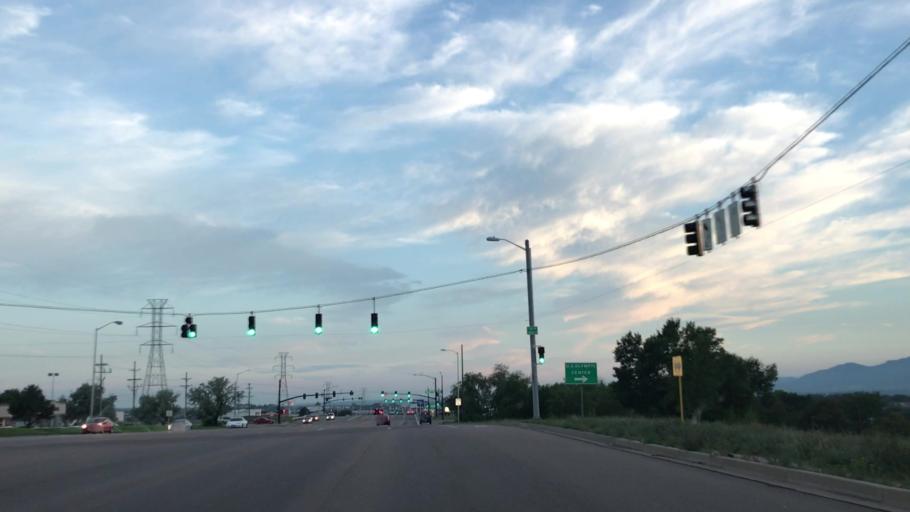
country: US
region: Colorado
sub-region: El Paso County
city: Cimarron Hills
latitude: 38.8422
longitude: -104.7576
